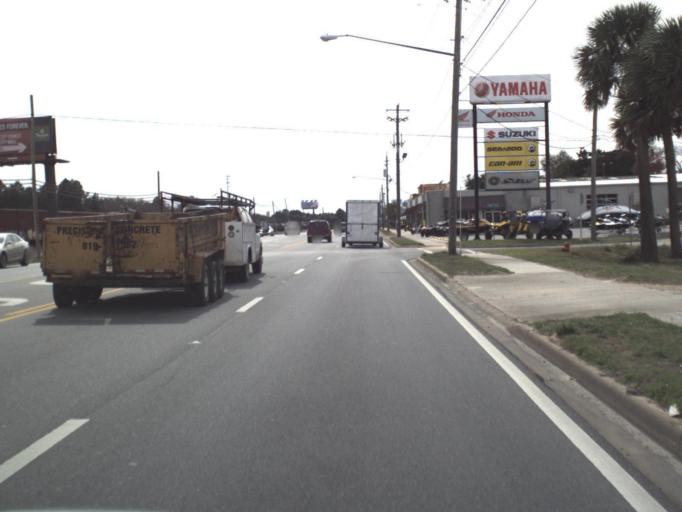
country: US
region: Florida
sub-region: Bay County
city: Hiland Park
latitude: 30.1923
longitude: -85.6370
